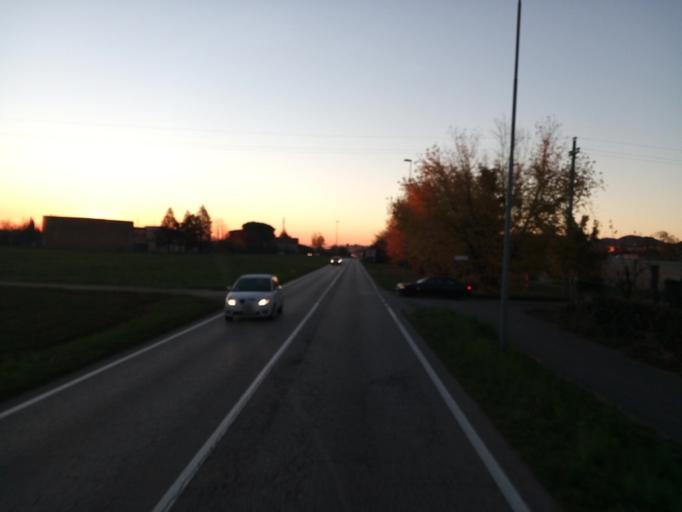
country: IT
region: Veneto
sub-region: Provincia di Vicenza
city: Schio
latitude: 45.6973
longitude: 11.3683
